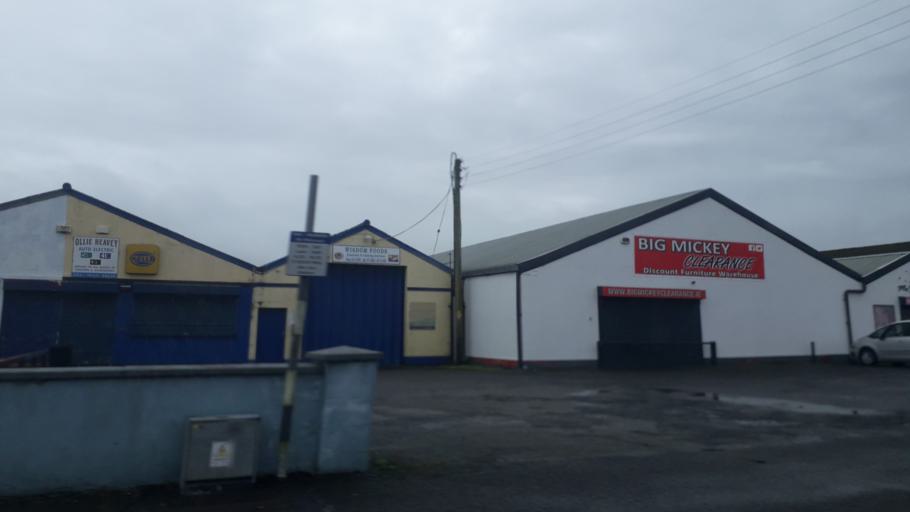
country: IE
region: Leinster
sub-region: An Longfort
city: Longford
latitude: 53.7279
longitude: -7.8063
